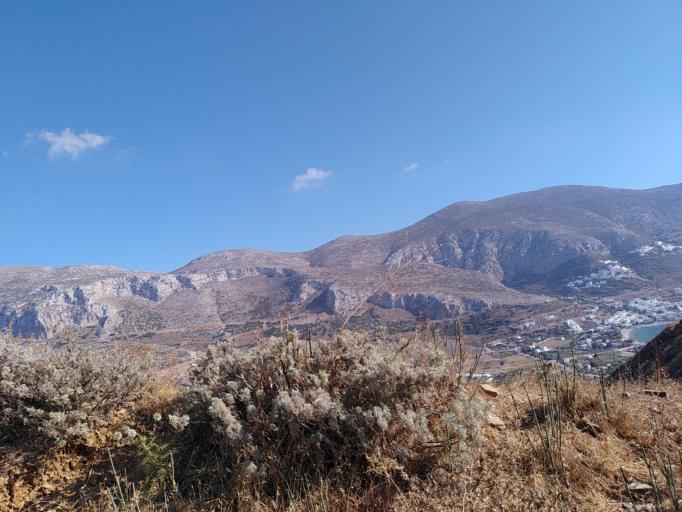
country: GR
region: South Aegean
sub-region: Nomos Kykladon
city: Amorgos
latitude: 36.9142
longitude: 25.9795
